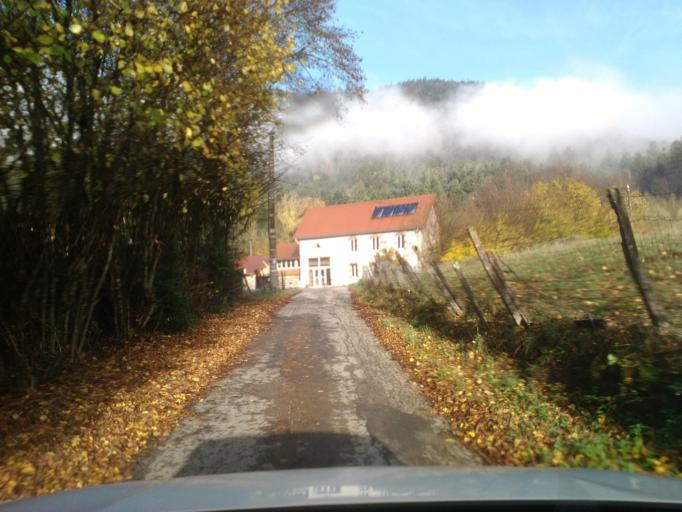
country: FR
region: Lorraine
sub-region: Departement des Vosges
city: Senones
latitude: 48.4201
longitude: 6.9998
